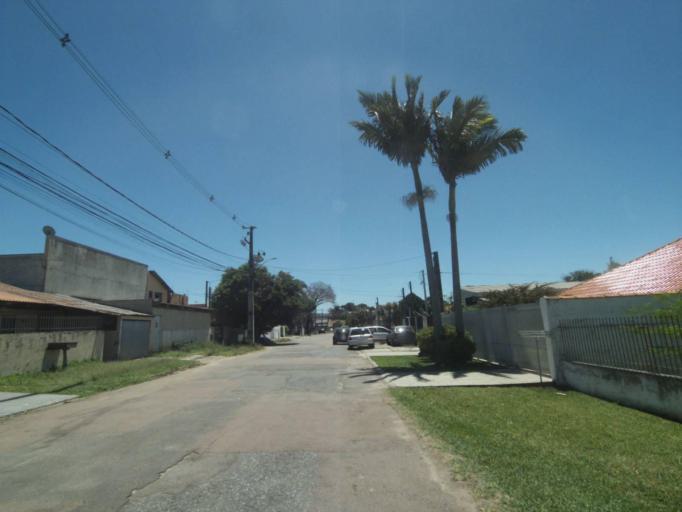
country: BR
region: Parana
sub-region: Curitiba
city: Curitiba
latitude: -25.4870
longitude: -49.3454
